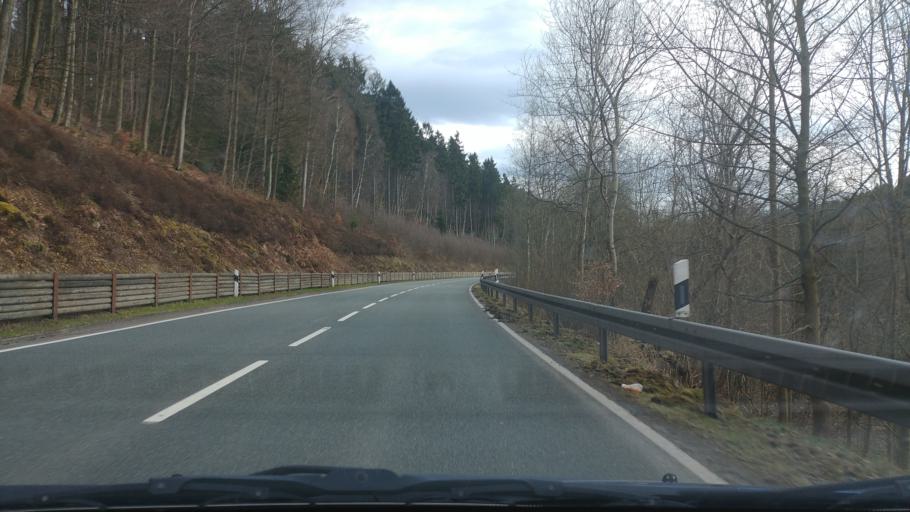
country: DE
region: Lower Saxony
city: Bevern
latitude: 51.8130
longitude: 9.4935
